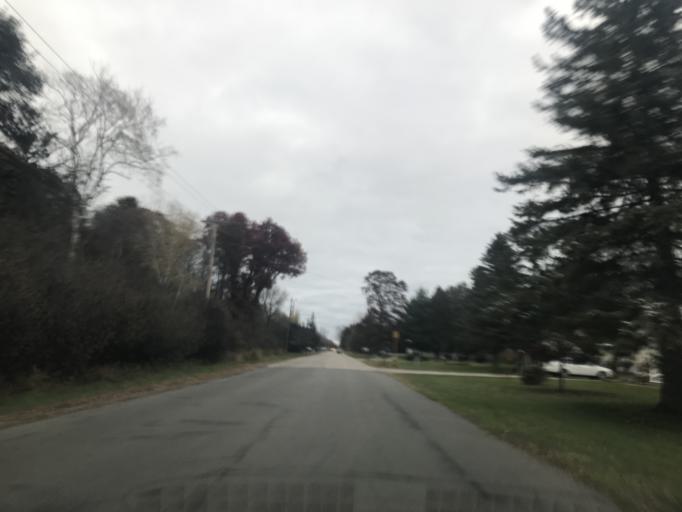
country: US
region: Wisconsin
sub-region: Marinette County
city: Marinette
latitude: 45.0934
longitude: -87.6574
